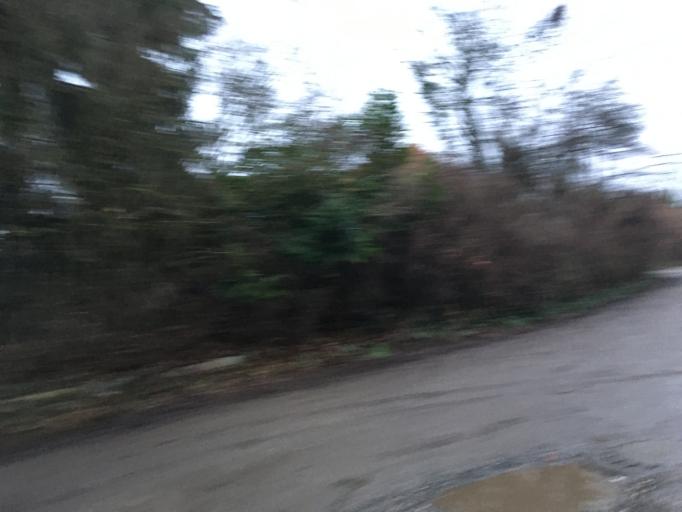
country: DE
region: Berlin
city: Niederschonhausen
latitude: 52.5924
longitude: 13.4082
